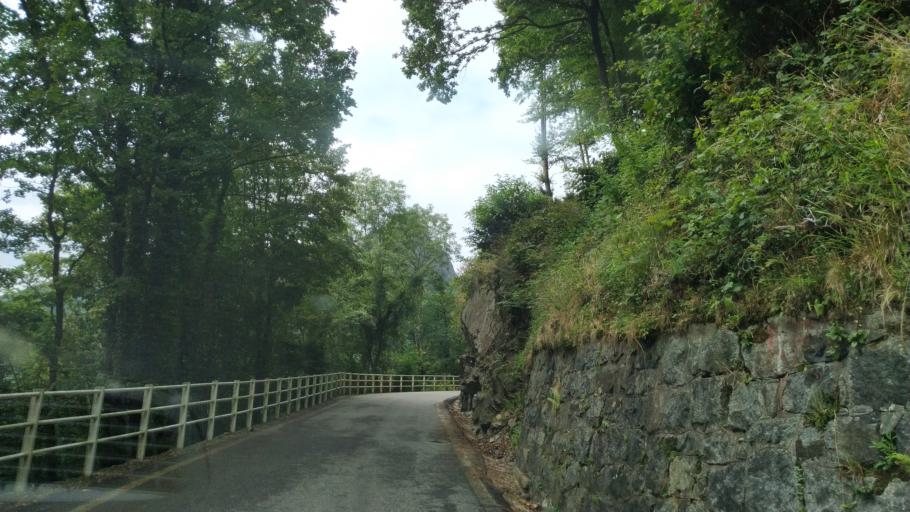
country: IT
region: Piedmont
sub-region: Provincia di Vercelli
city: Sabbia
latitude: 45.8578
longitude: 8.2414
